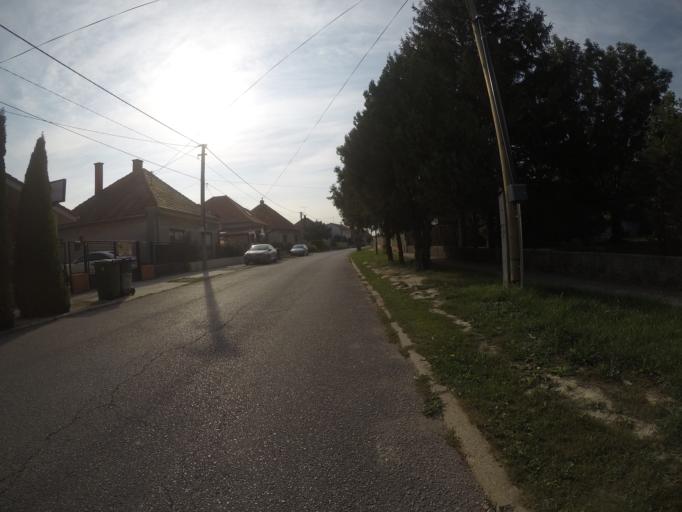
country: SK
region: Trnavsky
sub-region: Okres Dunajska Streda
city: Velky Meder
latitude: 47.8549
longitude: 17.7608
